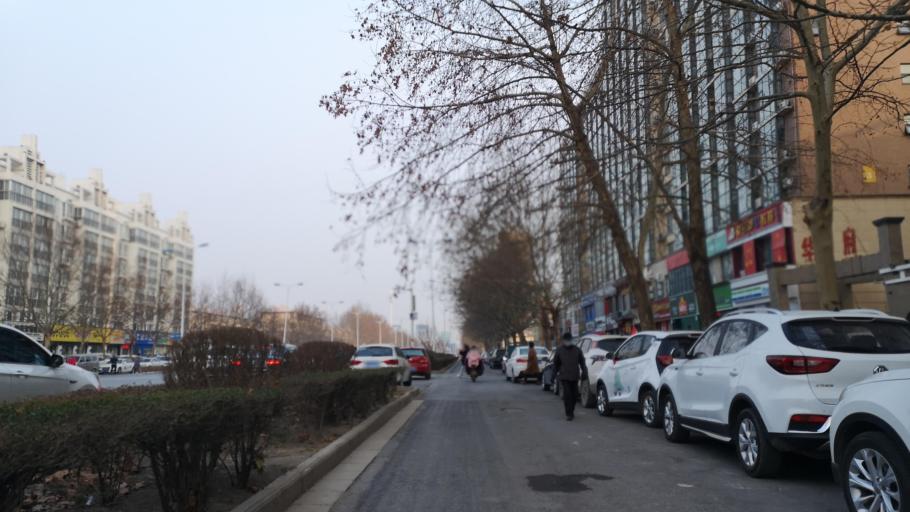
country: CN
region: Henan Sheng
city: Zhongyuanlu
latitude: 35.7653
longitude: 115.0923
